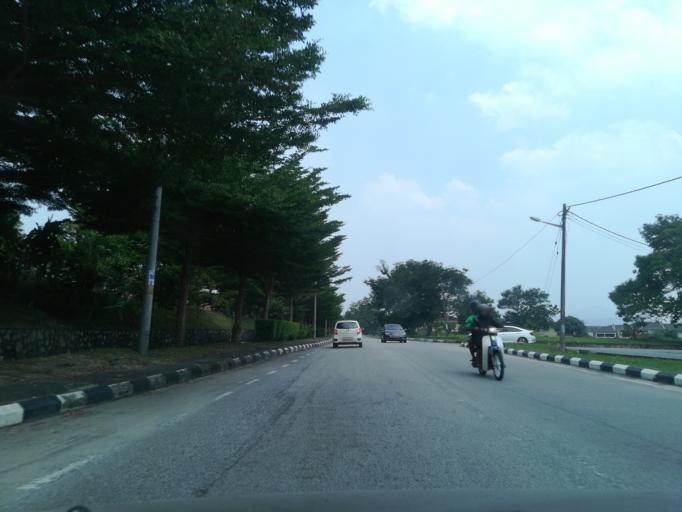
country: MY
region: Kedah
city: Kulim
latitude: 5.4014
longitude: 100.5670
